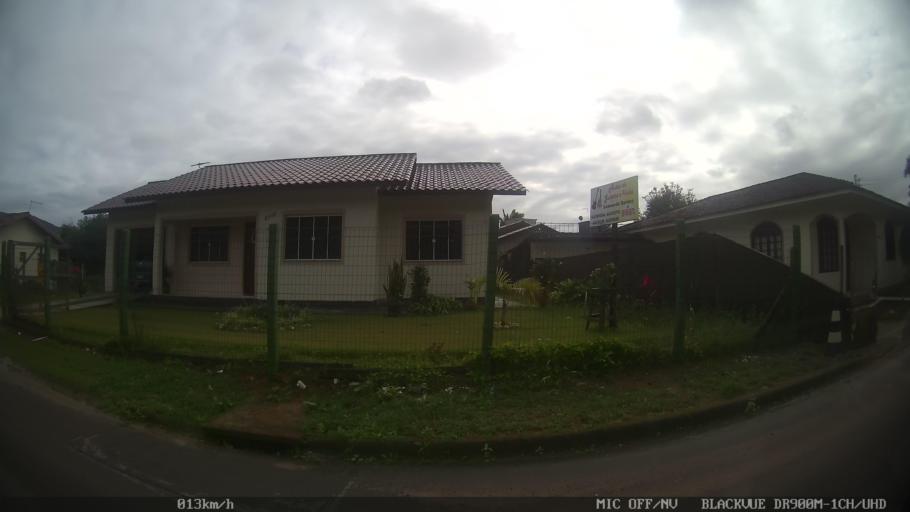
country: BR
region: Santa Catarina
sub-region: Biguacu
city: Biguacu
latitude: -27.5184
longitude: -48.6479
